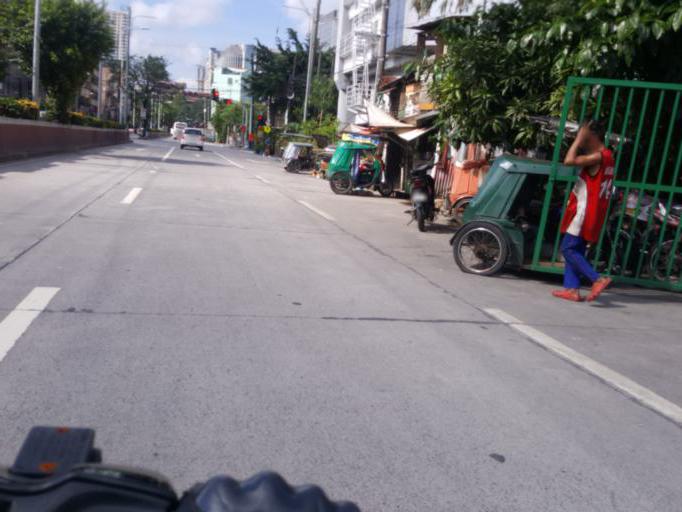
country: PH
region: Metro Manila
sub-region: City of Manila
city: Manila
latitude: 14.6133
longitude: 120.9864
